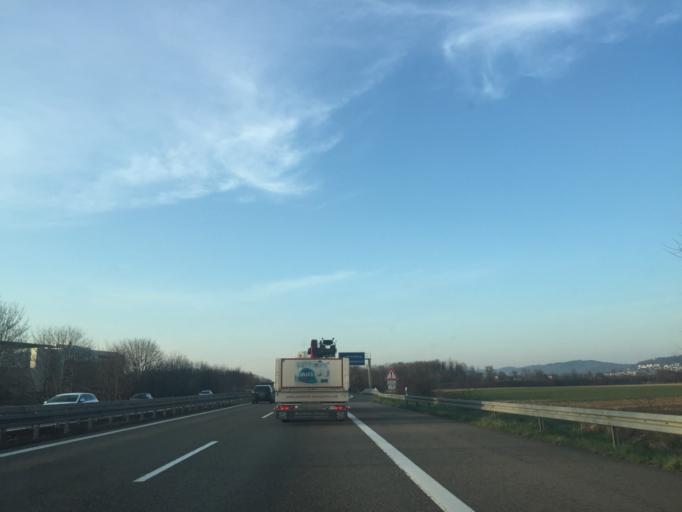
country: DE
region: Baden-Wuerttemberg
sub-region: Karlsruhe Region
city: Heddesheim
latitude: 49.5044
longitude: 8.6400
